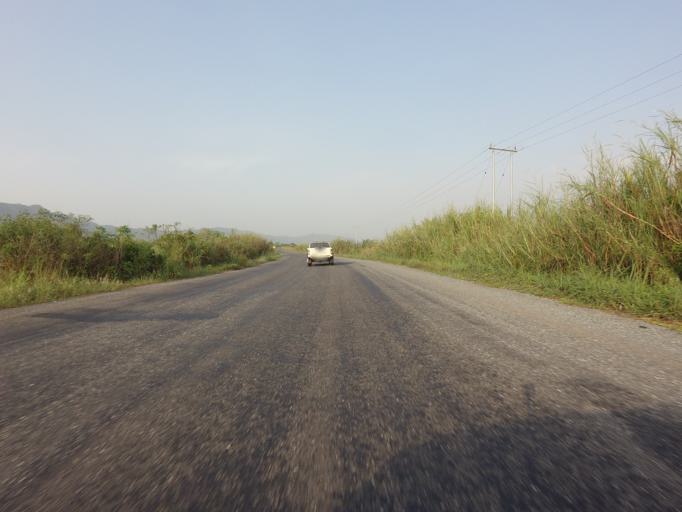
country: GH
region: Volta
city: Ho
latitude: 6.4526
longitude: 0.2134
